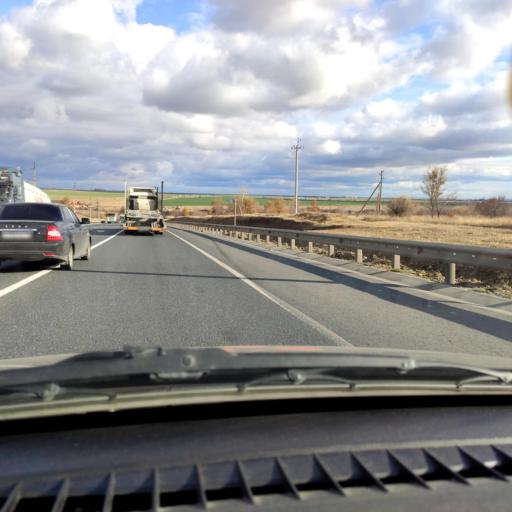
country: RU
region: Samara
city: Varlamovo
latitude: 53.1991
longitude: 48.3748
